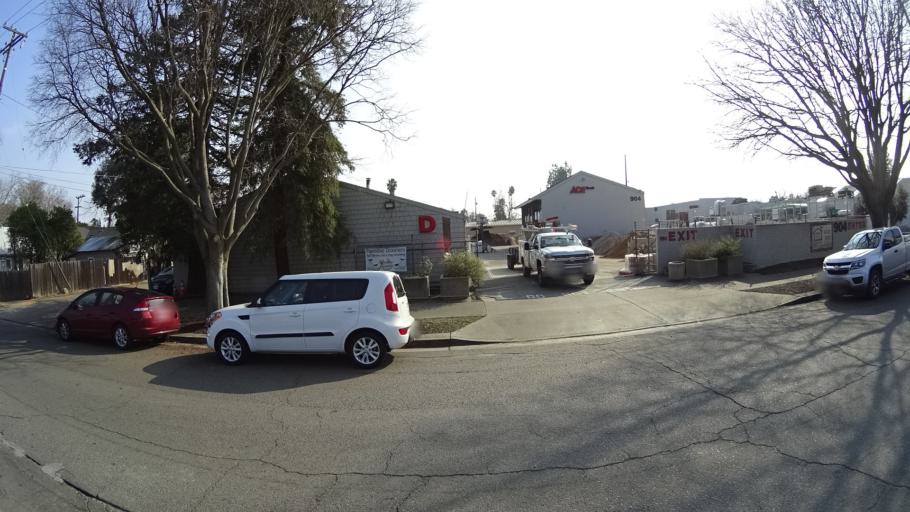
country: US
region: California
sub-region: Yolo County
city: Davis
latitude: 38.5465
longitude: -121.7382
